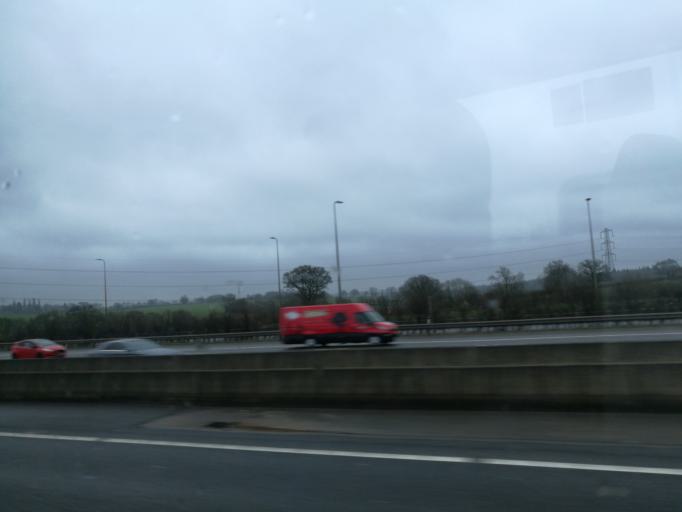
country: GB
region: England
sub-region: Hertfordshire
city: Redbourn
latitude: 51.7633
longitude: -0.4166
